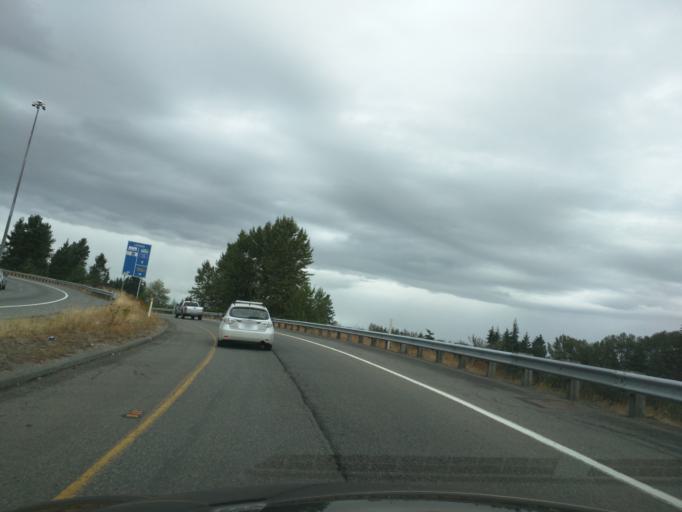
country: US
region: Washington
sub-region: Snohomish County
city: Mill Creek
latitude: 47.9165
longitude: -122.2055
